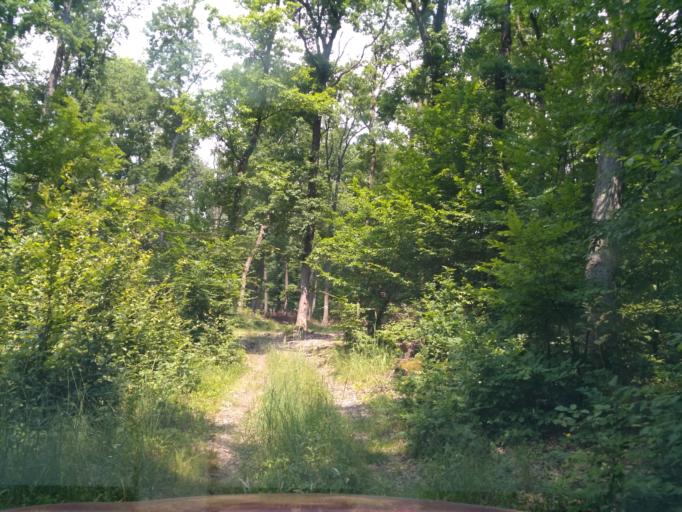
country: SK
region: Kosicky
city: Moldava nad Bodvou
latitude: 48.6421
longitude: 21.0390
